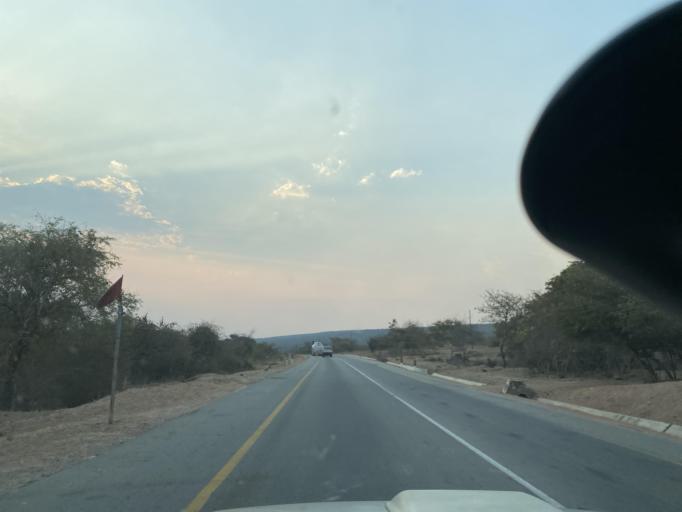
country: ZM
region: Lusaka
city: Kafue
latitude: -15.9001
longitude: 28.3451
